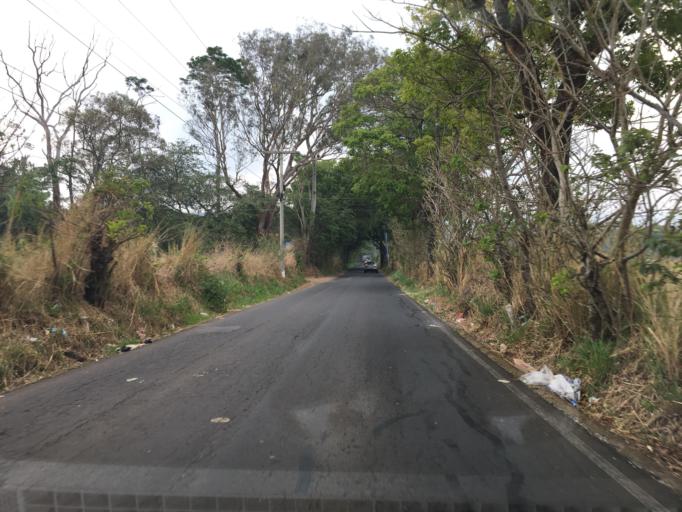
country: GT
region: Guatemala
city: Fraijanes
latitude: 14.3894
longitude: -90.4875
